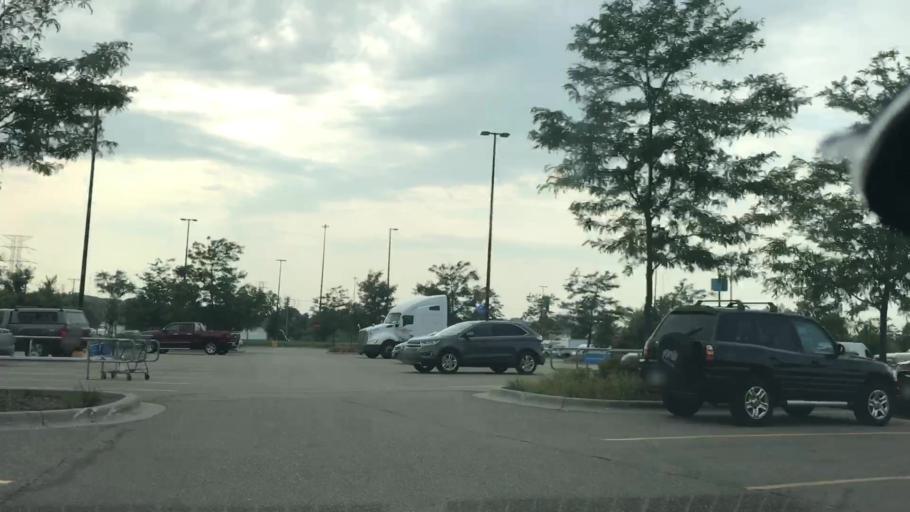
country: US
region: Minnesota
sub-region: Ramsey County
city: Lauderdale
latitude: 45.0210
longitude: -93.1848
